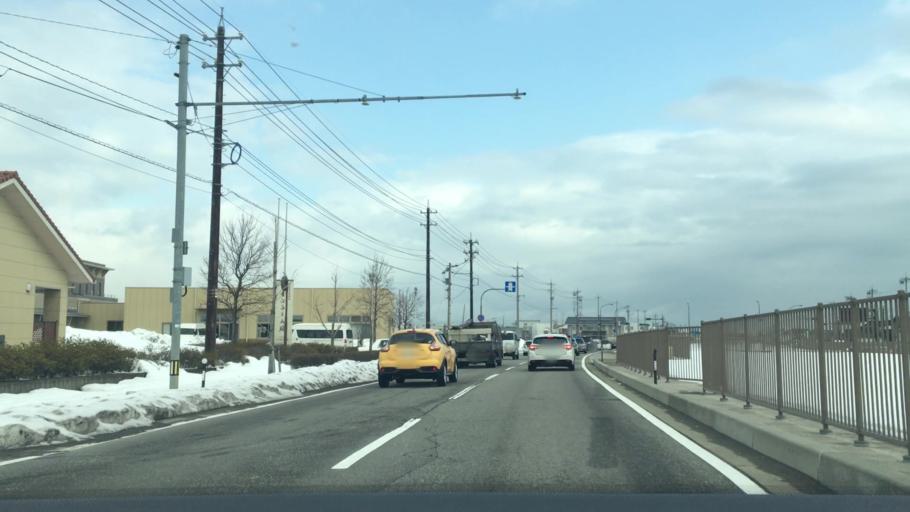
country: JP
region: Ishikawa
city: Matsuto
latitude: 36.5581
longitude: 136.5792
